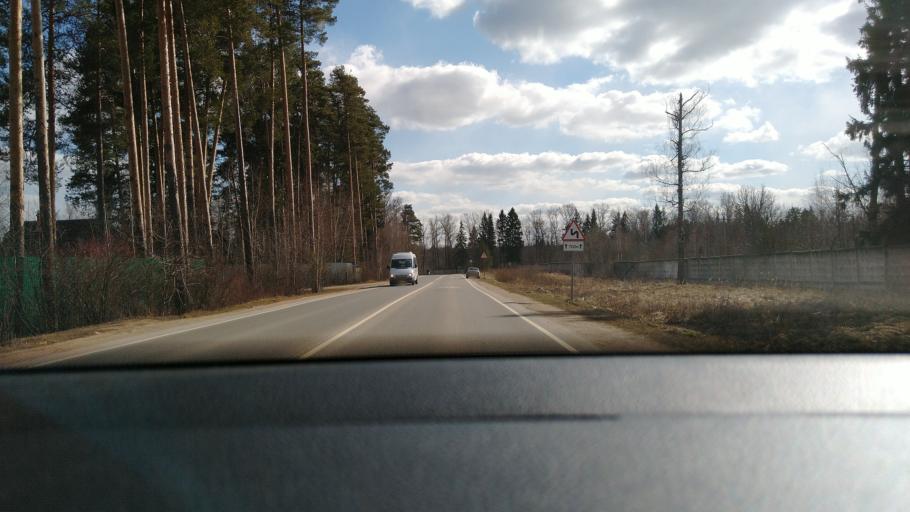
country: RU
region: Moskovskaya
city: Zvenigorod
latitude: 55.6495
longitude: 36.8210
